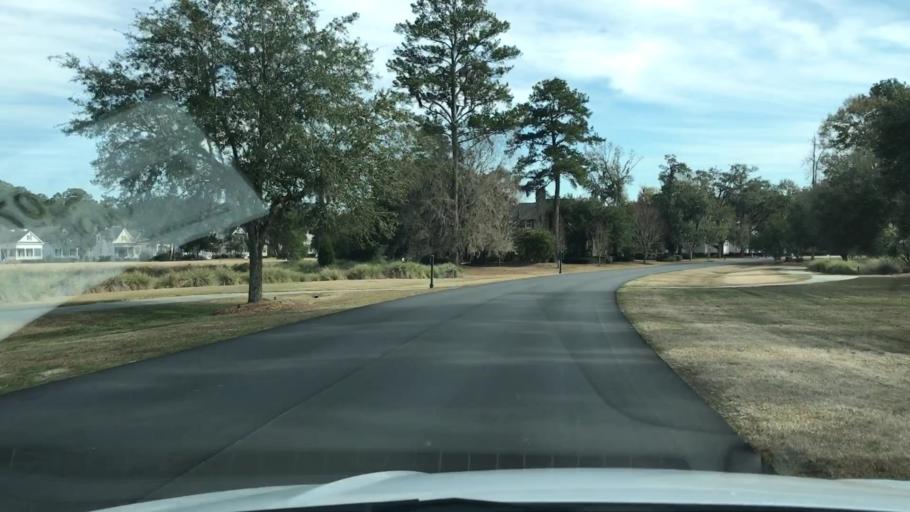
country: US
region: South Carolina
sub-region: Beaufort County
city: Bluffton
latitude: 32.3411
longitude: -80.9128
